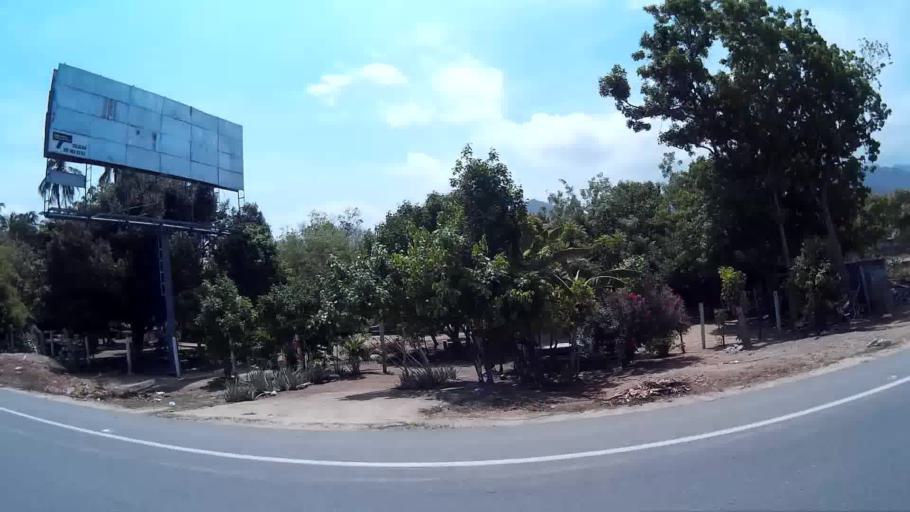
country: CO
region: Magdalena
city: Santa Marta
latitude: 11.1564
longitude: -74.2231
